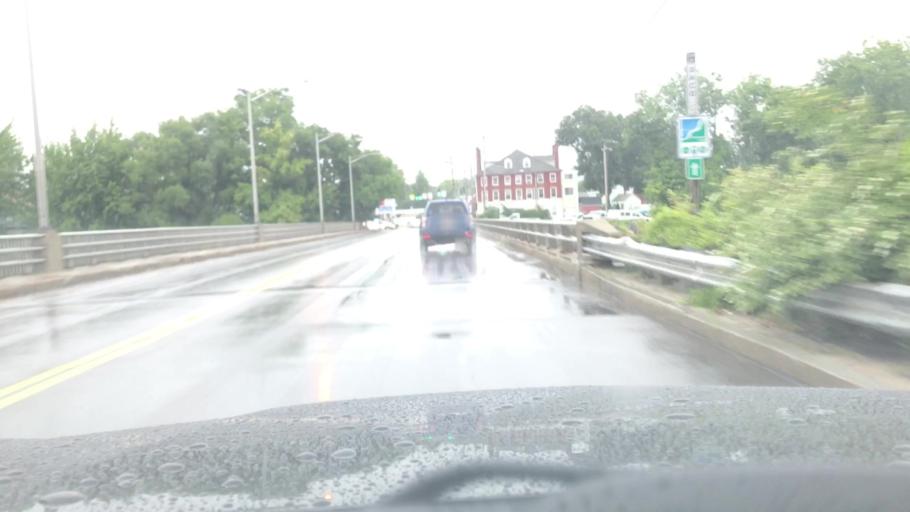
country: US
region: Maine
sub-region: York County
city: Biddeford
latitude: 43.4985
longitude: -70.4520
